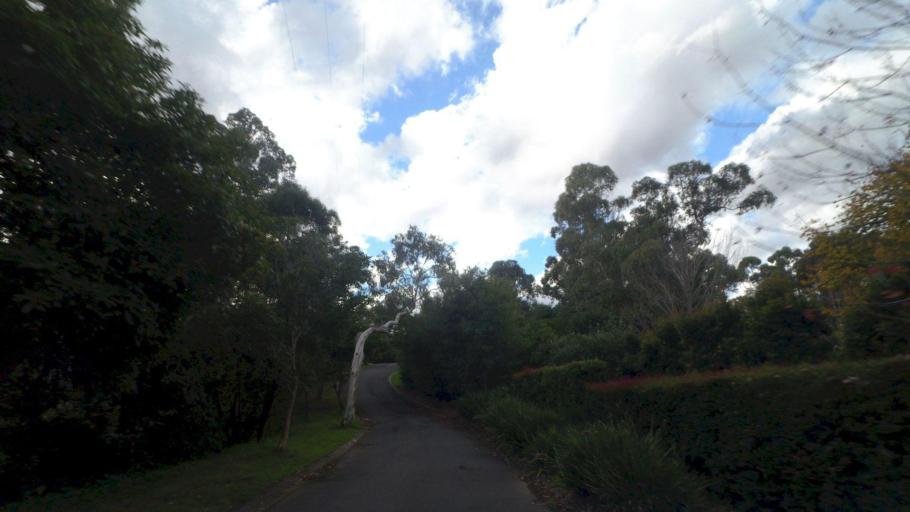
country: AU
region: Victoria
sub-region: Banyule
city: Lower Plenty
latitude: -37.7380
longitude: 145.1292
